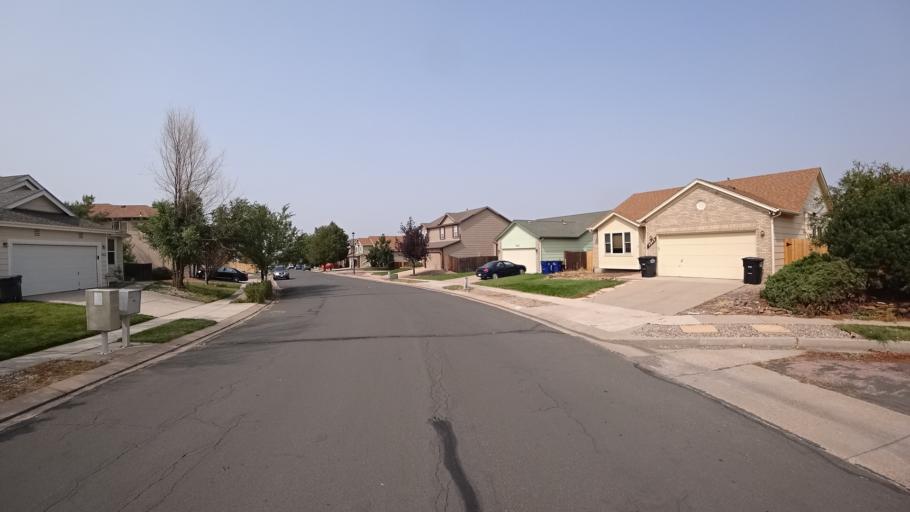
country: US
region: Colorado
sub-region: El Paso County
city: Cimarron Hills
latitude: 38.9169
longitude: -104.7302
